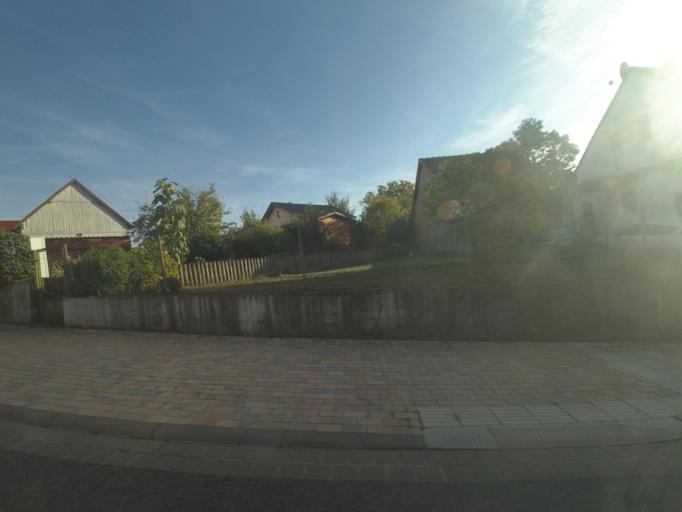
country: DE
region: Hesse
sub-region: Regierungsbezirk Darmstadt
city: Birstein
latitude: 50.3154
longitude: 9.3354
